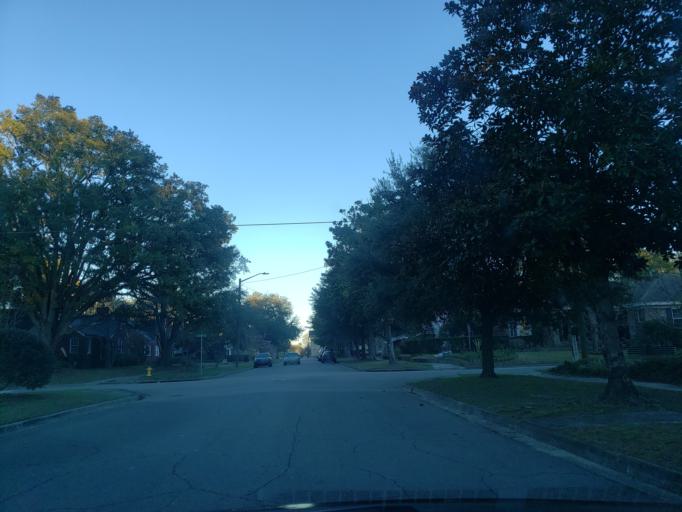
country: US
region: Georgia
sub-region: Chatham County
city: Thunderbolt
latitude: 32.0388
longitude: -81.0912
